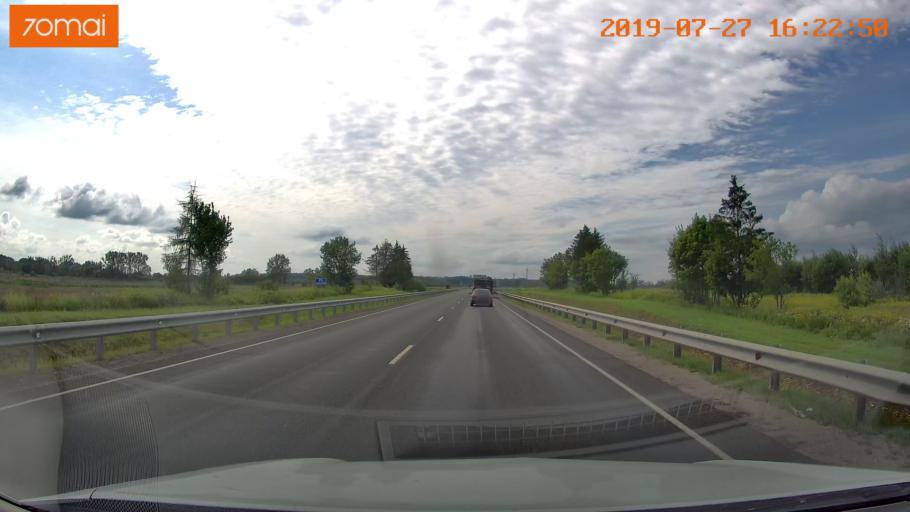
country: RU
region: Kaliningrad
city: Zheleznodorozhnyy
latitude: 54.6294
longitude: 21.4859
